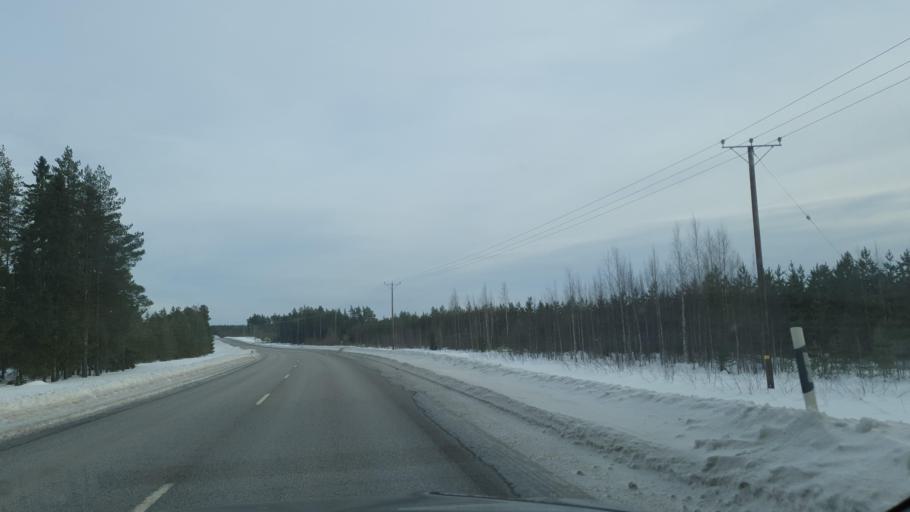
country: FI
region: Kainuu
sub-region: Kajaani
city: Vaala
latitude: 64.5376
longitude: 27.1982
